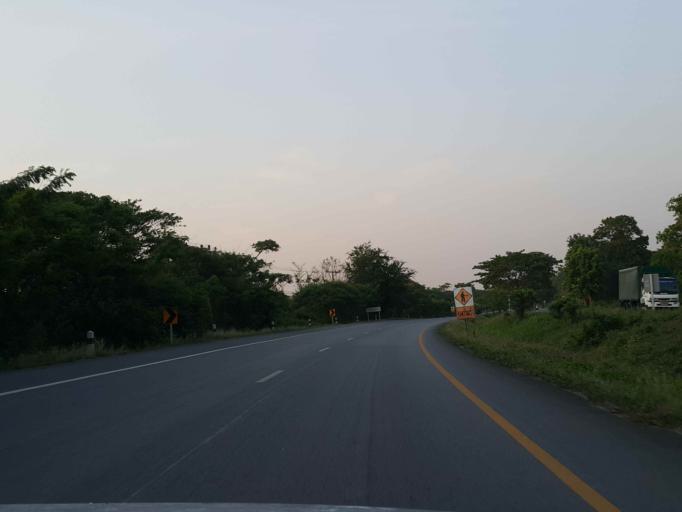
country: TH
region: Lampang
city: Sop Prap
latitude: 17.9132
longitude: 99.3420
